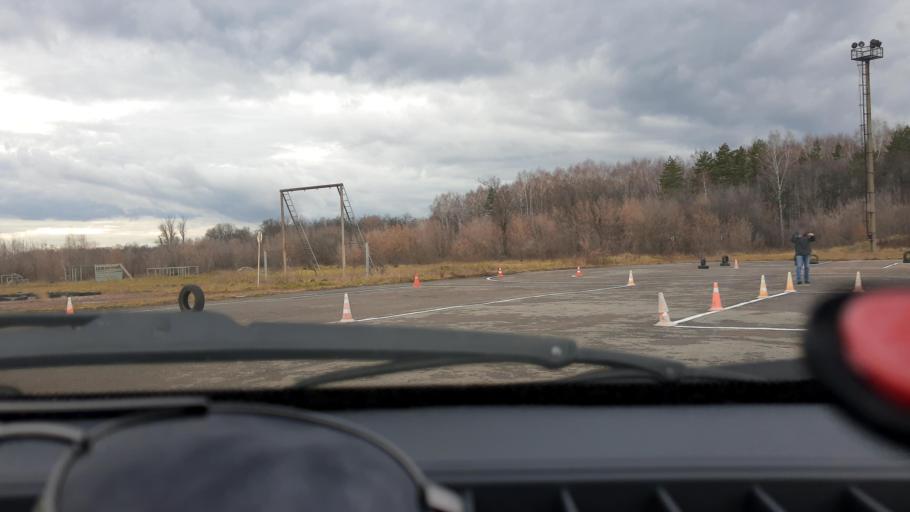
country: RU
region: Bashkortostan
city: Ufa
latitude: 54.7855
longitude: 56.1597
